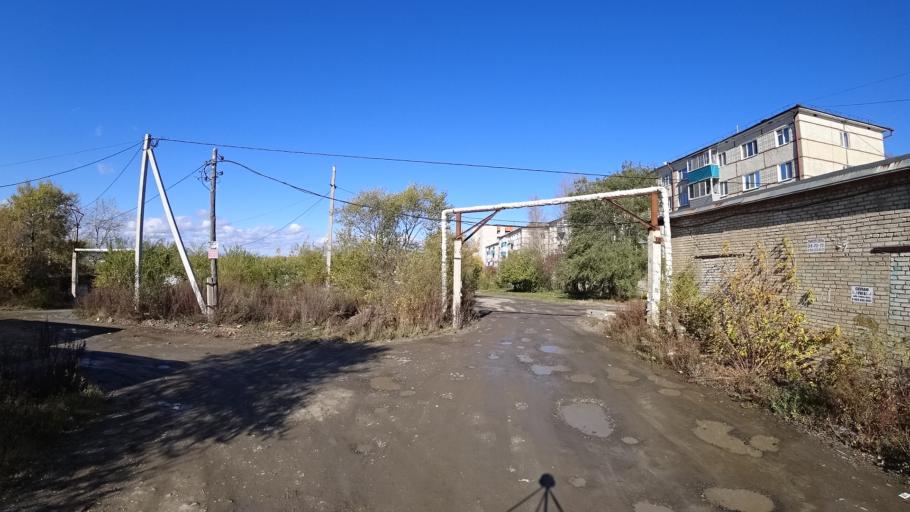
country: RU
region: Khabarovsk Krai
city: Amursk
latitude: 50.2202
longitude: 136.9013
